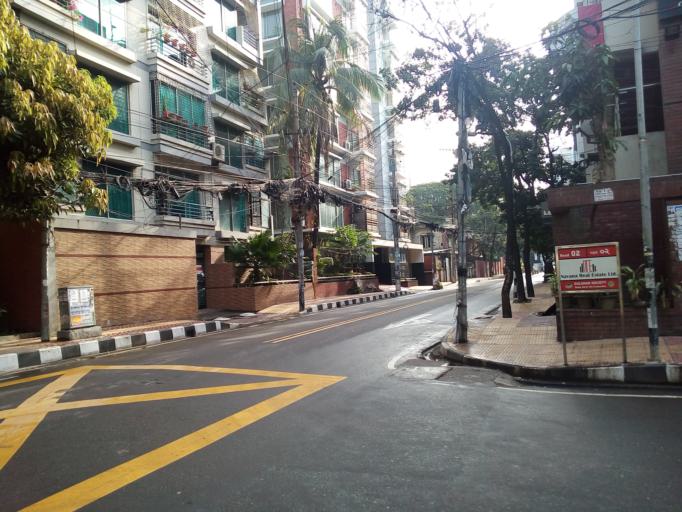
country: BD
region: Dhaka
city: Paltan
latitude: 23.7780
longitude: 90.4152
